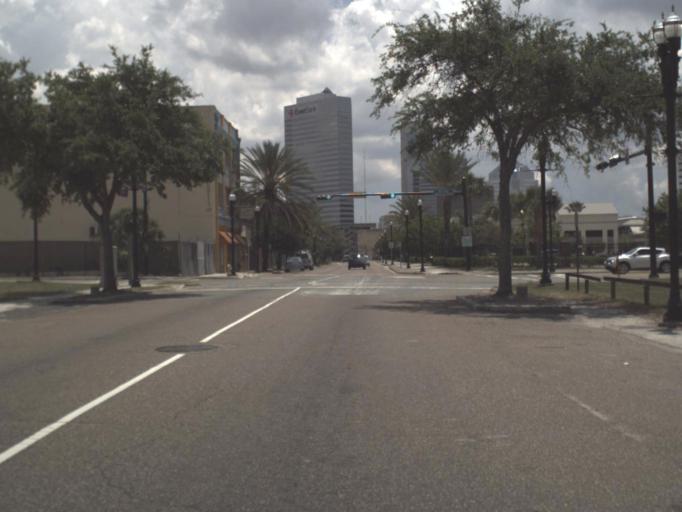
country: US
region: Florida
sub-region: Duval County
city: Jacksonville
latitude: 30.3291
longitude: -81.6707
